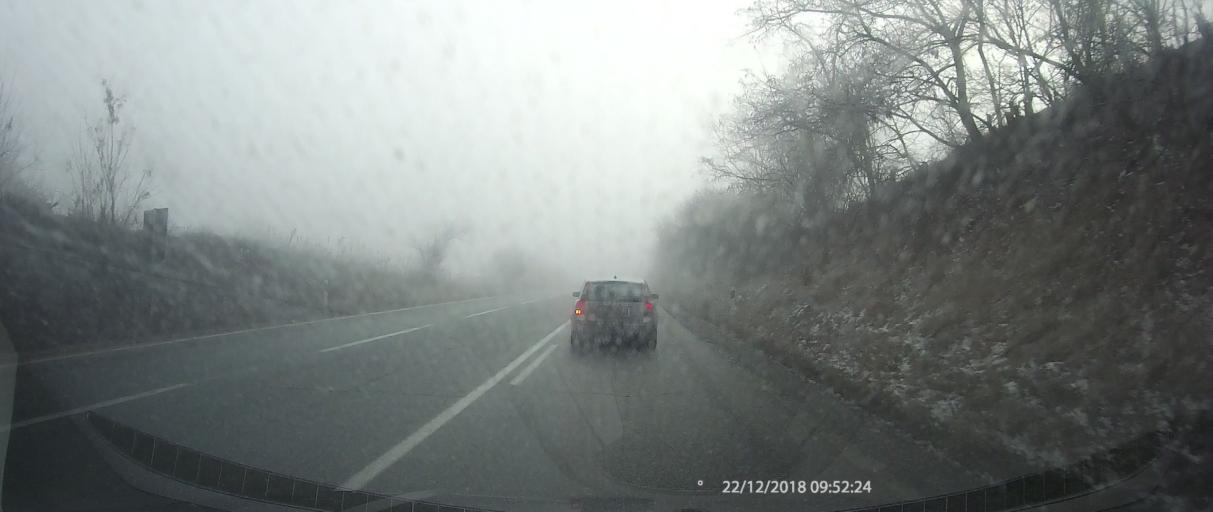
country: MK
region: Staro Nagoricane
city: Staro Nagorichane
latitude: 42.1690
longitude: 21.8226
